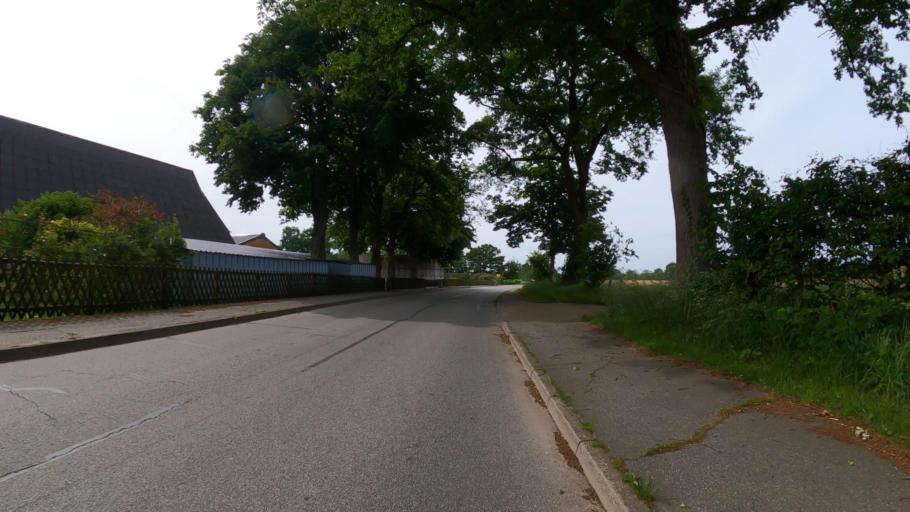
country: DE
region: Schleswig-Holstein
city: Sievershutten
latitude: 53.8445
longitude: 10.0977
